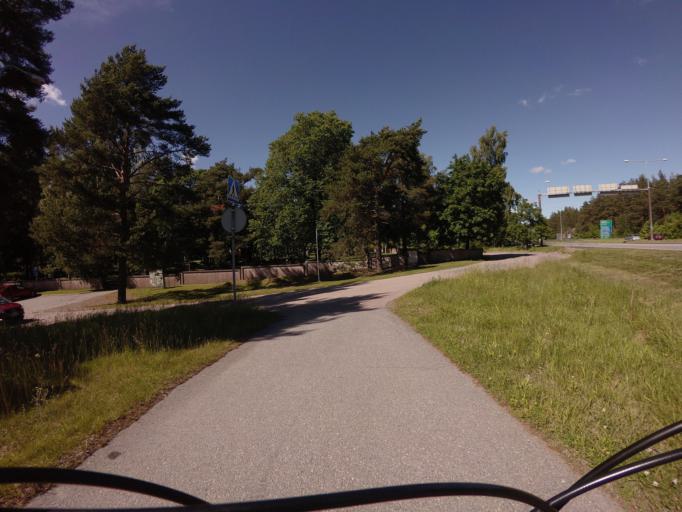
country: FI
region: Varsinais-Suomi
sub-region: Turku
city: Turku
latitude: 60.4909
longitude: 22.2801
